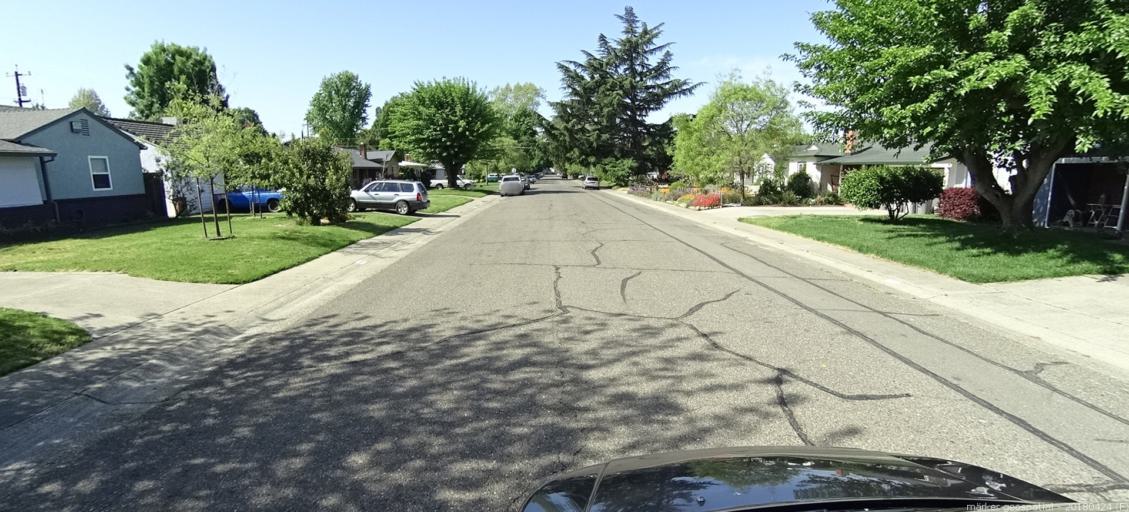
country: US
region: California
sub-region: Yolo County
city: West Sacramento
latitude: 38.5659
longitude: -121.5336
